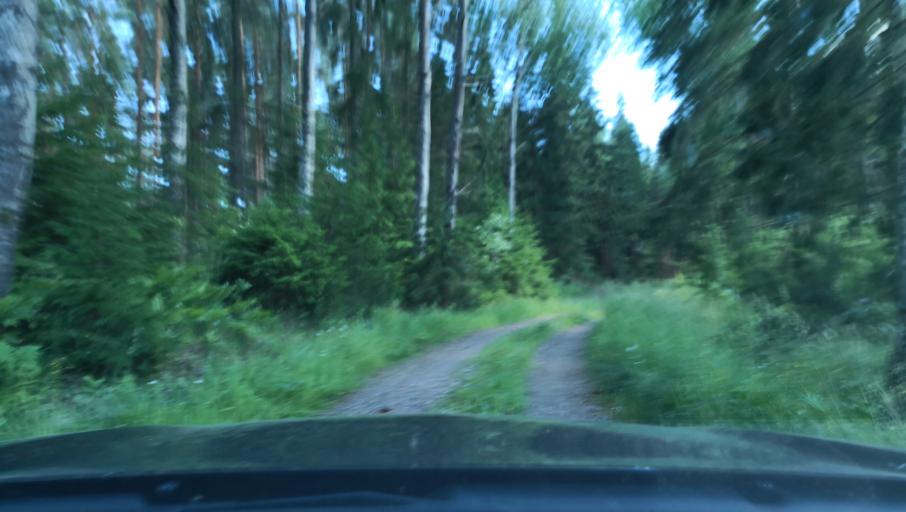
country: SE
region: Vaestmanland
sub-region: Kungsors Kommun
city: Kungsoer
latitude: 59.3418
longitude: 16.0604
